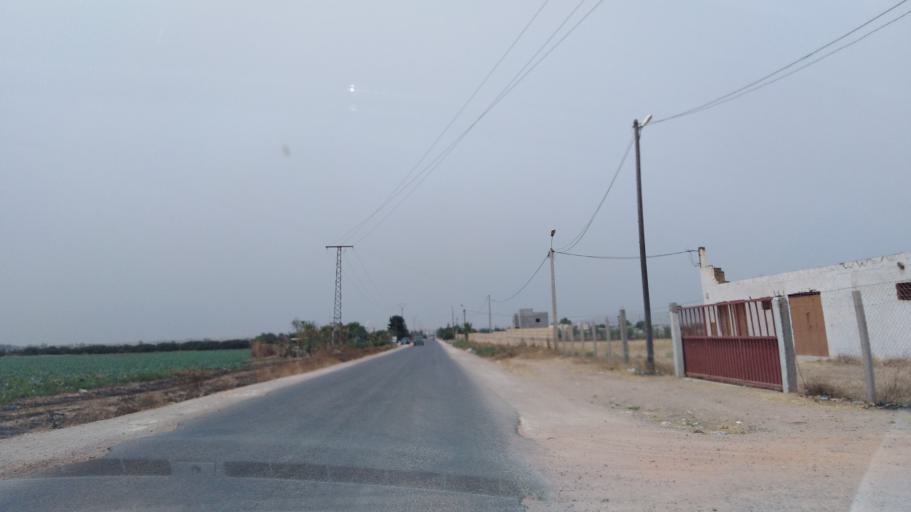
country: MA
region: Grand Casablanca
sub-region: Mediouna
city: Mediouna
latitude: 33.4163
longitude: -7.5173
